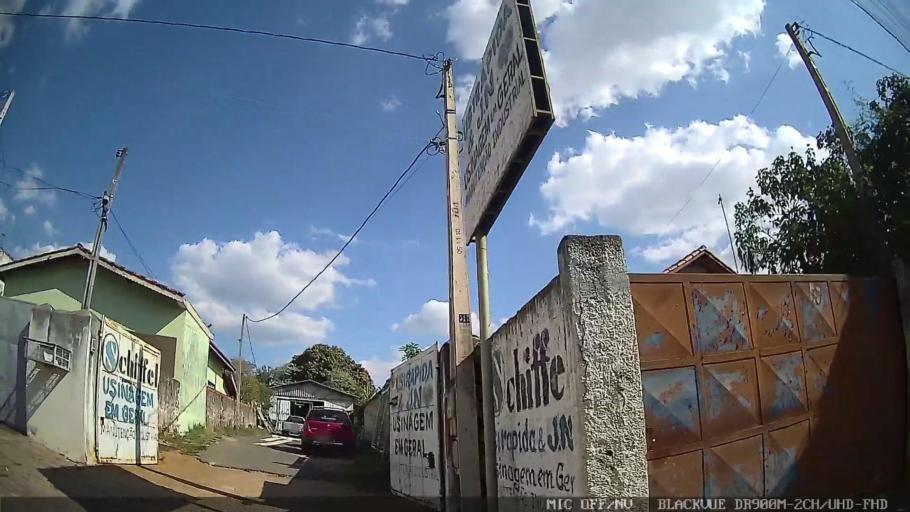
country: BR
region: Sao Paulo
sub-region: Itupeva
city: Itupeva
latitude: -23.2424
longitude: -47.0613
